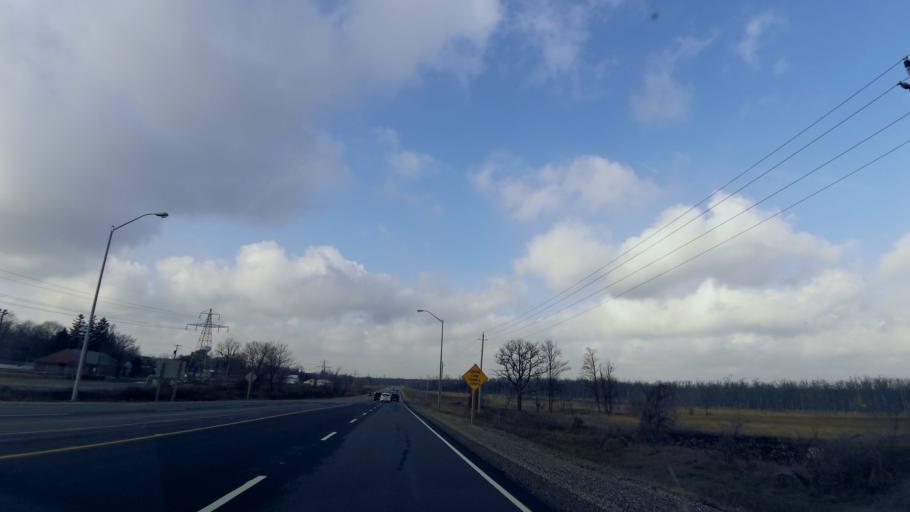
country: CA
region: Ontario
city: Ancaster
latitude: 43.4025
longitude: -80.0391
